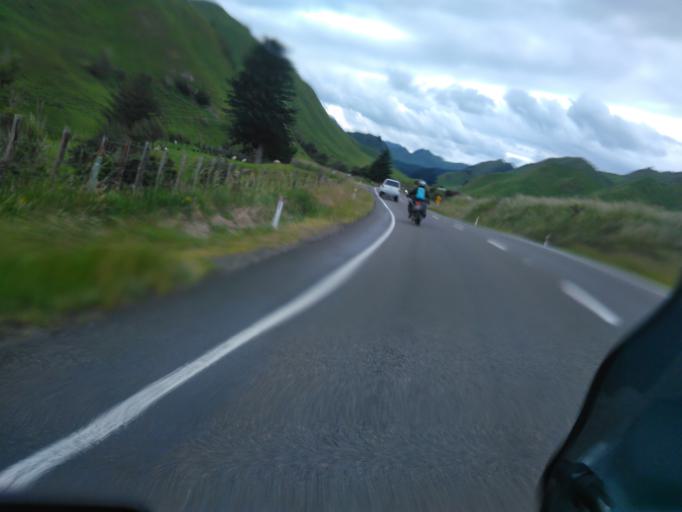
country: NZ
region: Bay of Plenty
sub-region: Opotiki District
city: Opotiki
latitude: -38.3646
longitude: 177.4623
